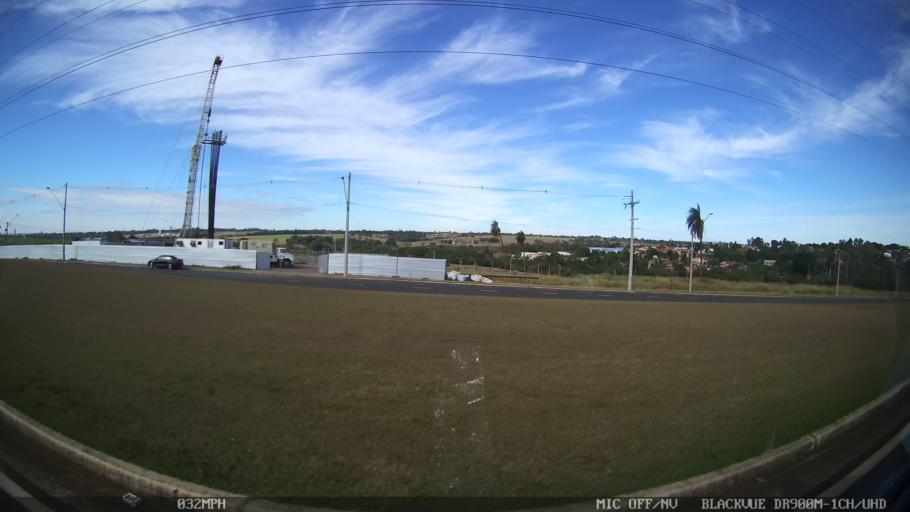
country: BR
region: Sao Paulo
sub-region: Sao Jose Do Rio Preto
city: Sao Jose do Rio Preto
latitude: -20.8575
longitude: -49.3798
